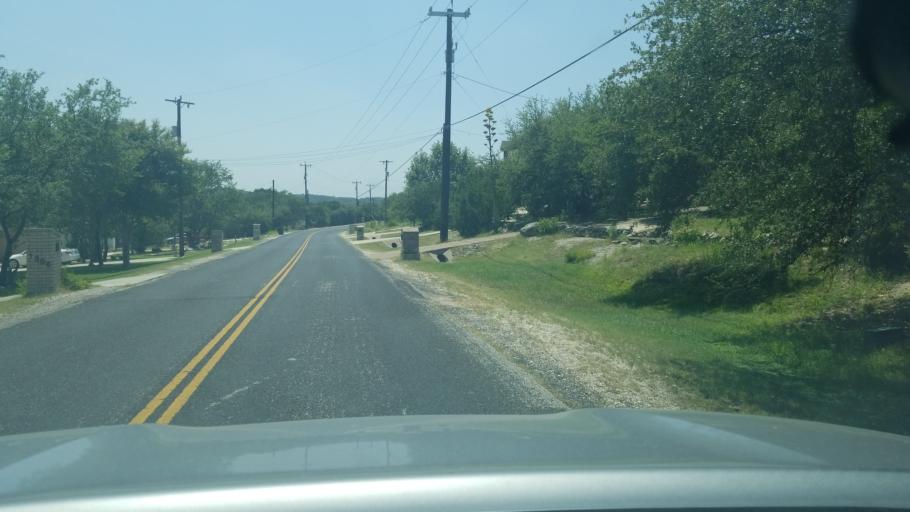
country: US
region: Texas
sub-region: Bexar County
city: Timberwood Park
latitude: 29.6775
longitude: -98.5168
